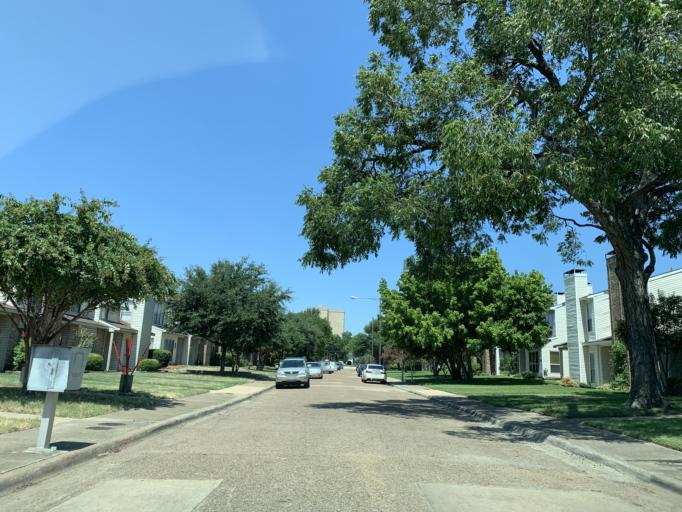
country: US
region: Texas
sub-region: Dallas County
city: Dallas
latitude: 32.7916
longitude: -96.7726
